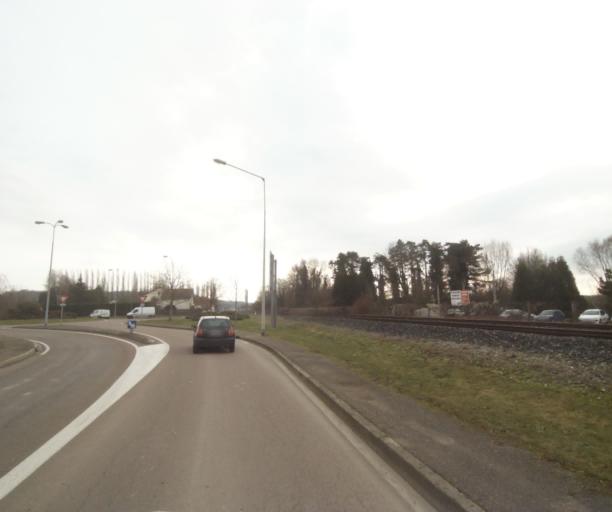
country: FR
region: Champagne-Ardenne
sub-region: Departement de la Haute-Marne
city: Bettancourt-la-Ferree
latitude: 48.6358
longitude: 4.9719
